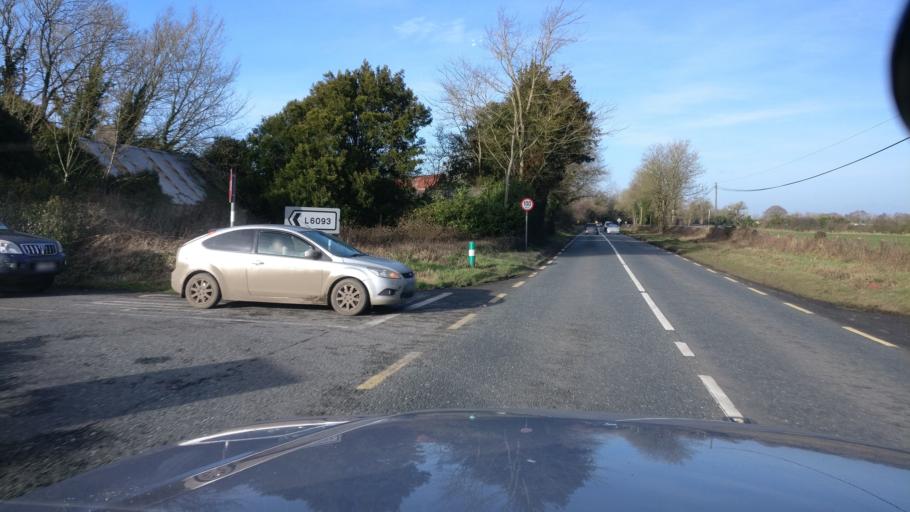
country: IE
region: Leinster
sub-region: Laois
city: Mountmellick
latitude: 53.1524
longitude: -7.3700
